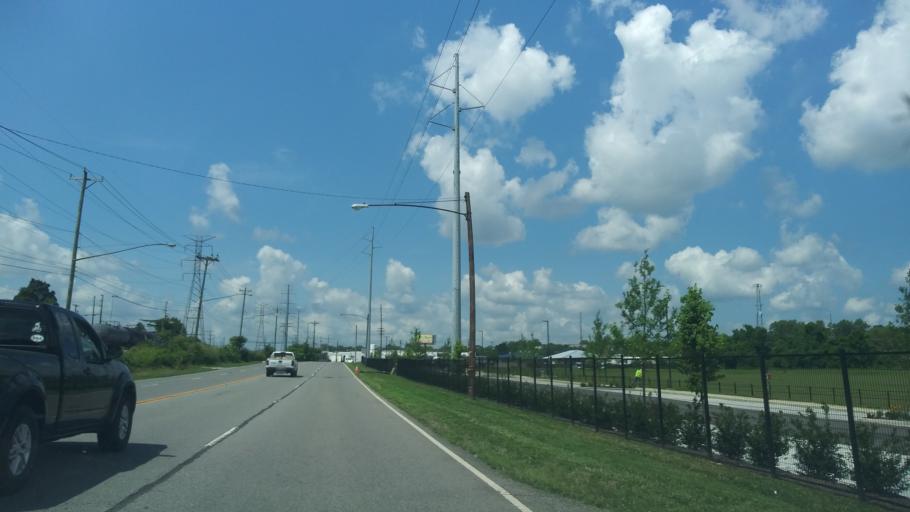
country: US
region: Tennessee
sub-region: Davidson County
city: Oak Hill
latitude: 36.1272
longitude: -86.7633
